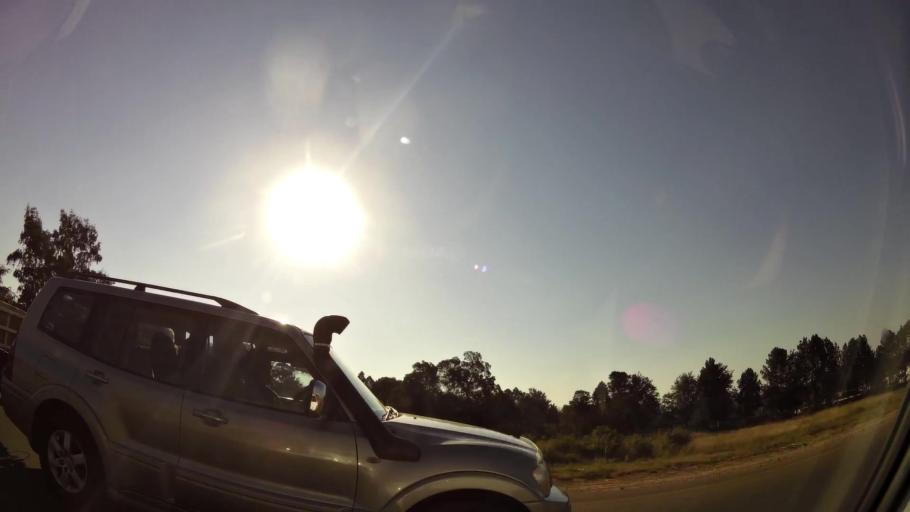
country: ZA
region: Gauteng
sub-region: City of Tshwane Metropolitan Municipality
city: Pretoria
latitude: -25.7768
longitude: 28.3461
